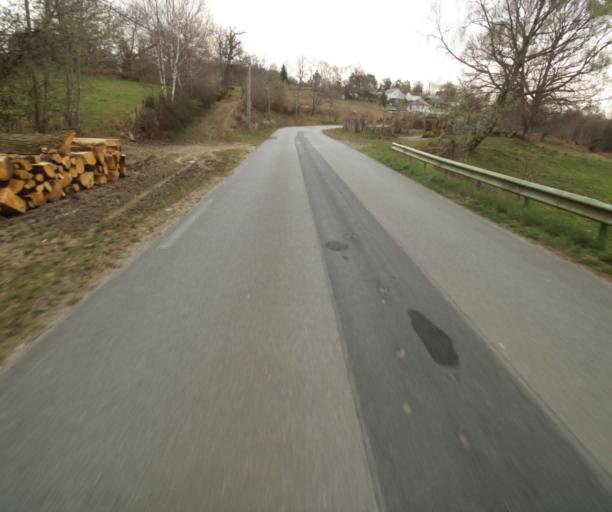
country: FR
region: Limousin
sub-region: Departement de la Correze
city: Correze
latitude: 45.4297
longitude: 1.8297
